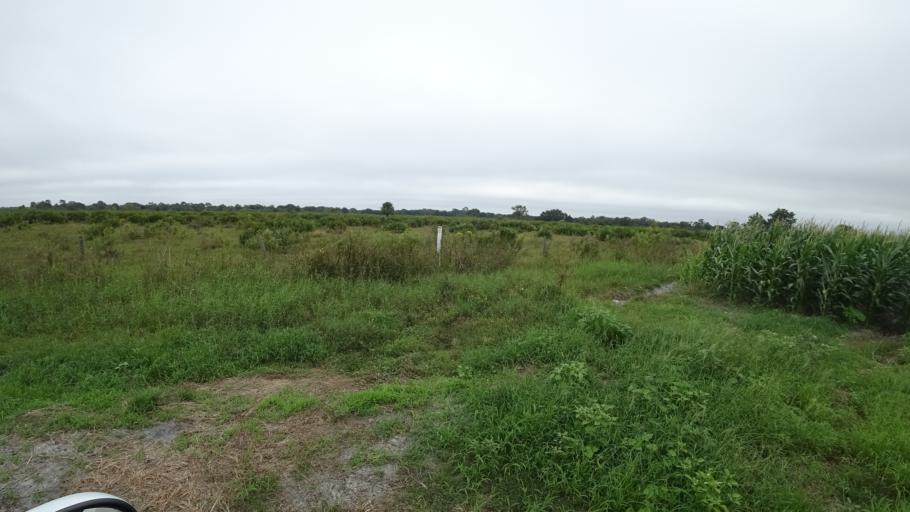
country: US
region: Florida
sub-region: DeSoto County
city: Nocatee
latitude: 27.2829
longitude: -82.1054
